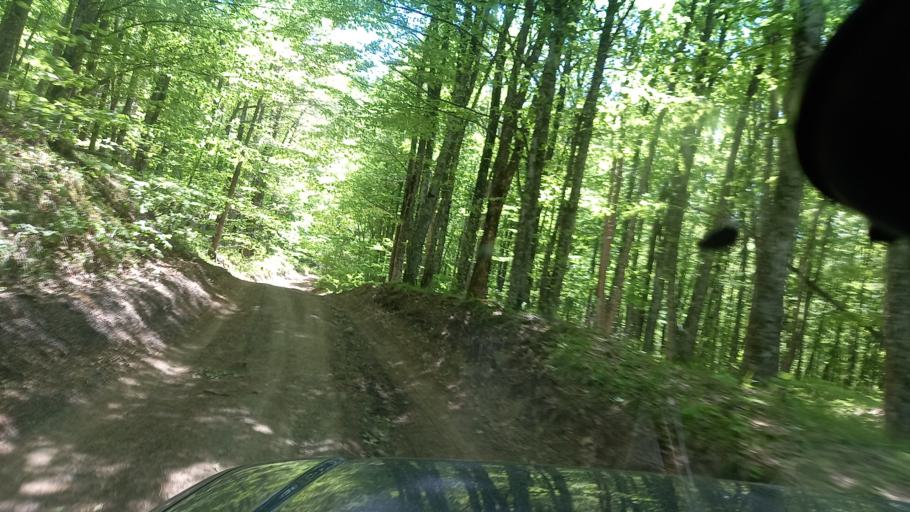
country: RU
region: Krasnodarskiy
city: Tuapse
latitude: 44.2541
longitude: 39.2846
